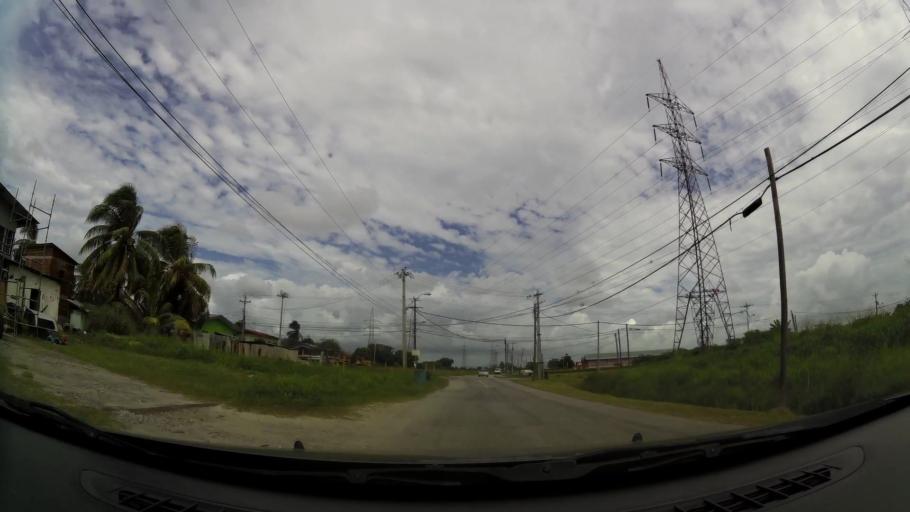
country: TT
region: Couva-Tabaquite-Talparo
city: Couva
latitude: 10.4028
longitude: -61.4644
